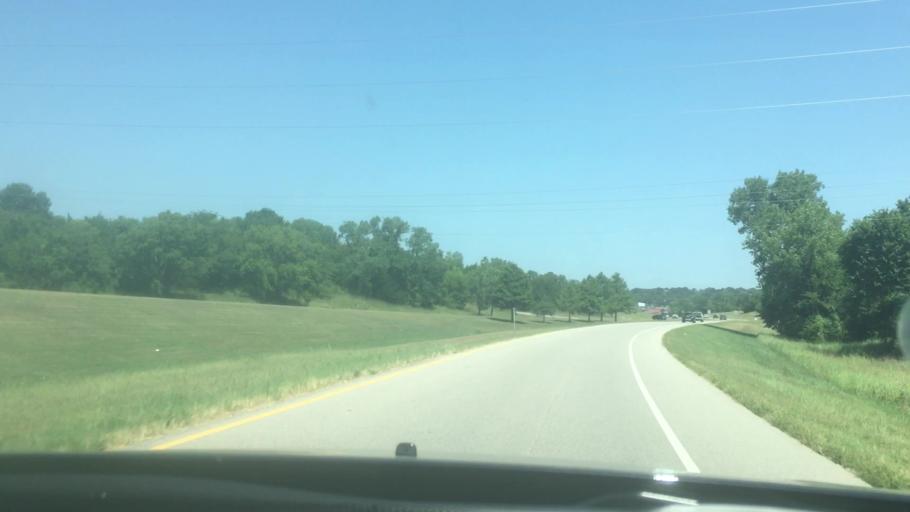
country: US
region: Oklahoma
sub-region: Pontotoc County
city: Ada
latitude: 34.7504
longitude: -96.6563
